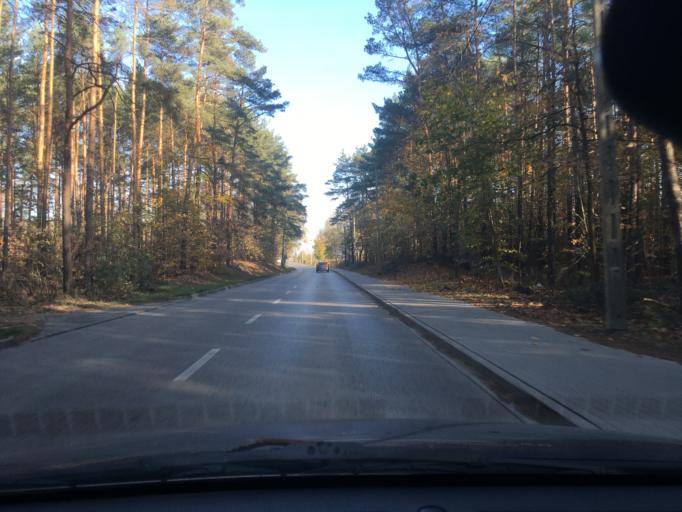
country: PL
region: Masovian Voivodeship
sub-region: Powiat piaseczynski
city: Lesznowola
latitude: 52.0804
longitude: 20.9386
